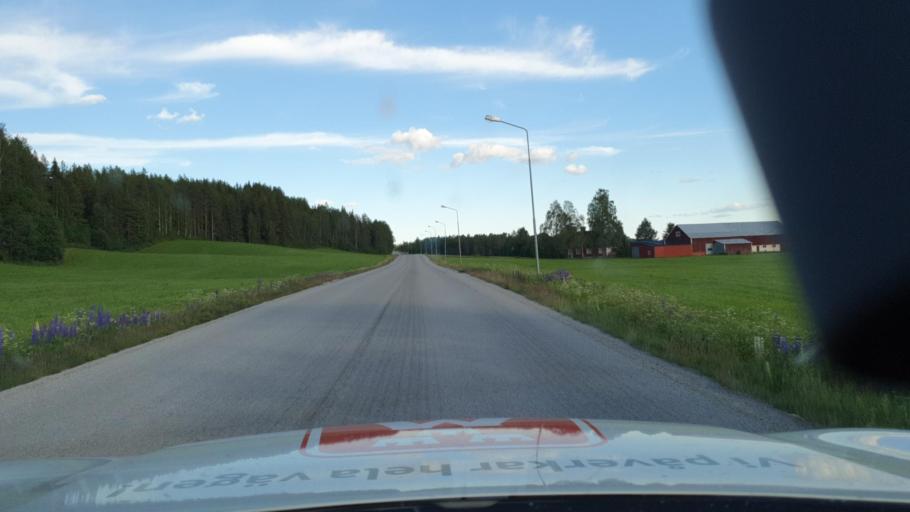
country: SE
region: Vaesterbotten
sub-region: Vindelns Kommun
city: Vindeln
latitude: 64.1367
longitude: 19.5265
